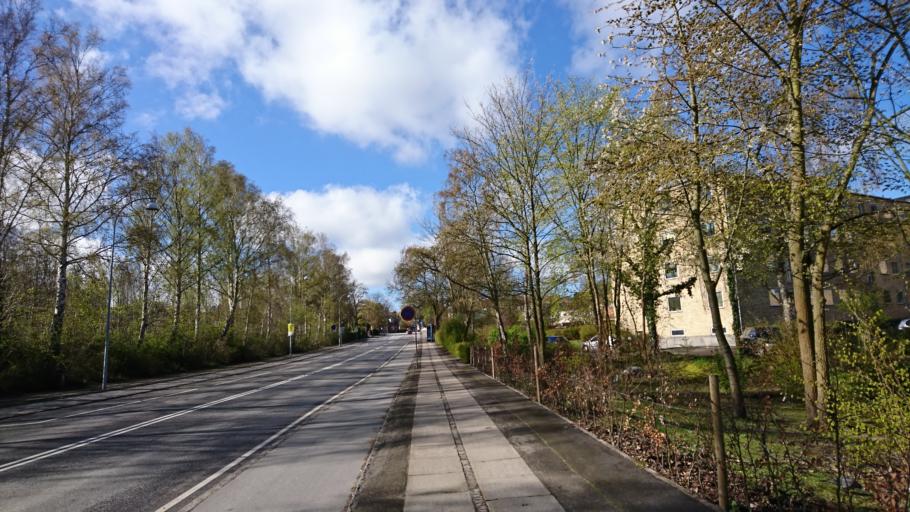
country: DK
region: Zealand
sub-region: Roskilde Kommune
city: Roskilde
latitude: 55.6467
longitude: 12.0781
